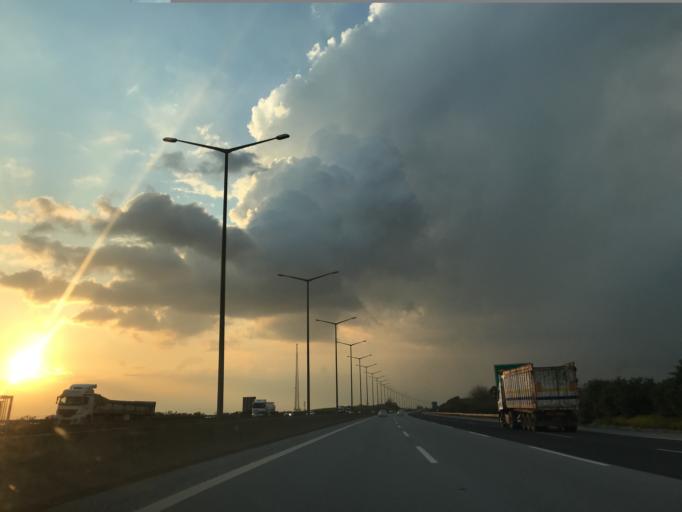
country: TR
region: Adana
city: Seyhan
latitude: 37.0315
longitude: 35.1908
